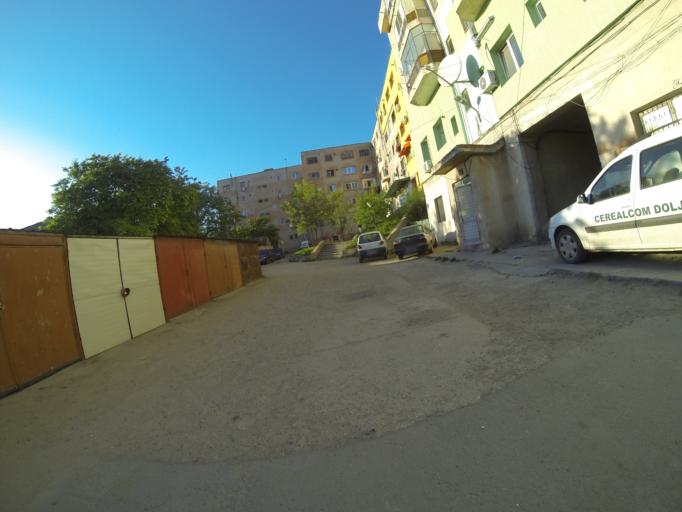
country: RO
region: Dolj
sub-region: Comuna Segarcea
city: Segarcea
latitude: 44.0941
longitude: 23.7454
